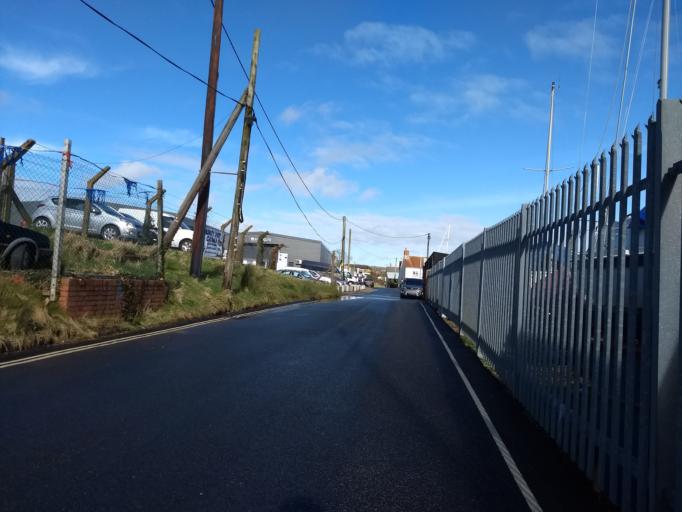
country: GB
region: England
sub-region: Isle of Wight
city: Newport
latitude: 50.7038
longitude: -1.2914
